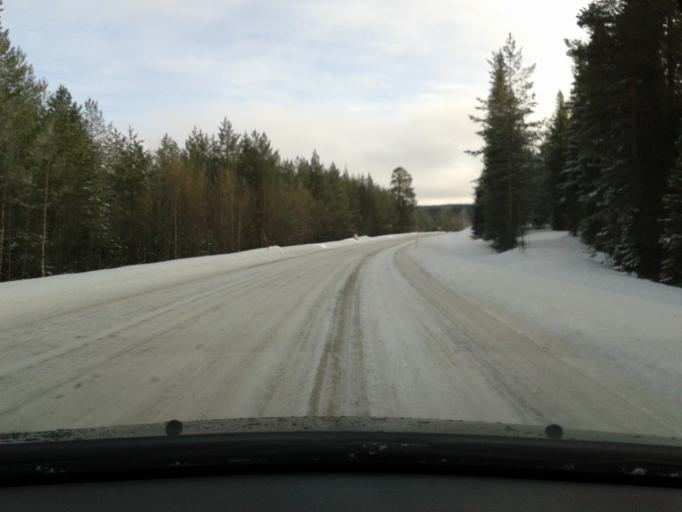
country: SE
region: Vaesterbotten
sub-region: Vilhelmina Kommun
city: Sjoberg
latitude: 64.7984
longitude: 16.0438
